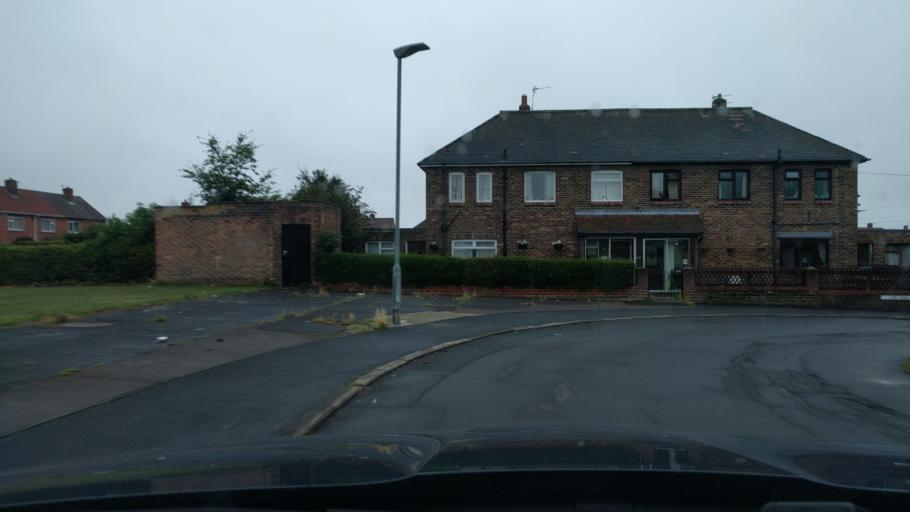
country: GB
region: England
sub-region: Northumberland
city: Bedlington
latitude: 55.1349
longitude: -1.5737
